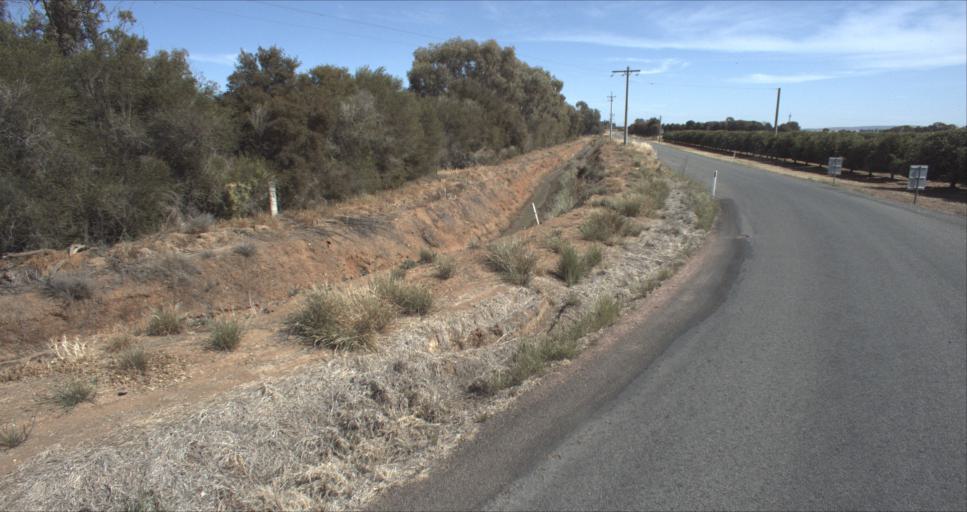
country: AU
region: New South Wales
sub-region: Leeton
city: Leeton
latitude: -34.5749
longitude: 146.4677
